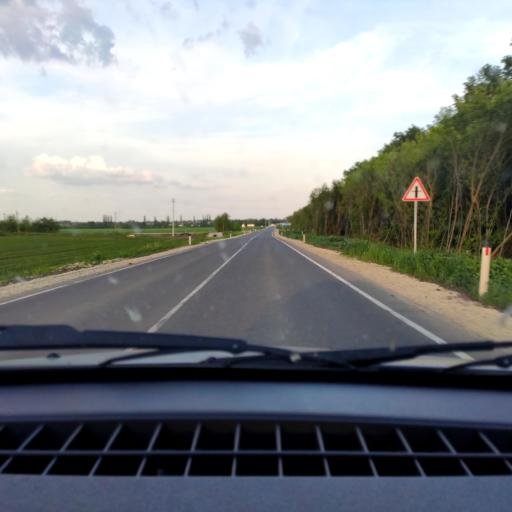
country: RU
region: Voronezj
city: Ramon'
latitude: 51.9214
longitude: 39.3050
